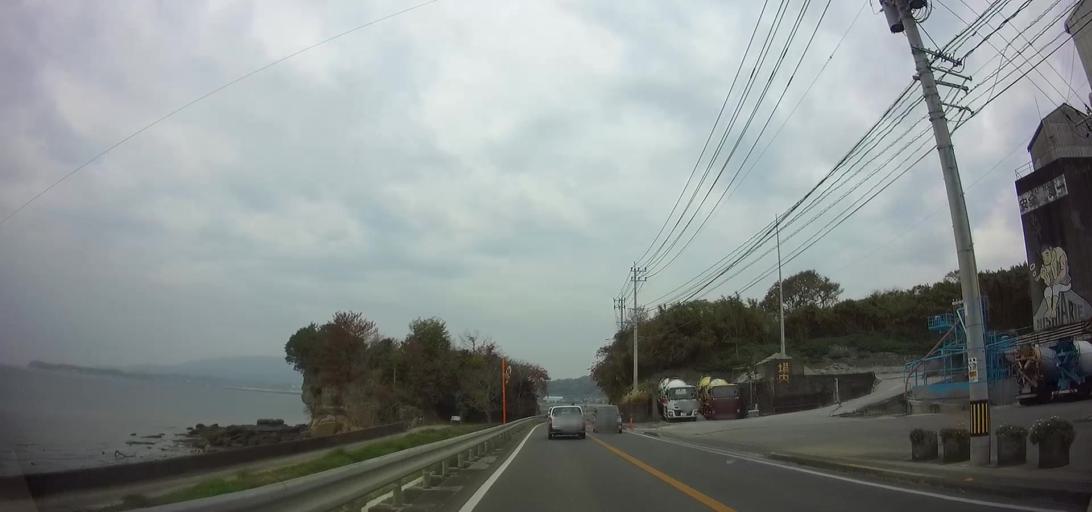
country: JP
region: Nagasaki
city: Shimabara
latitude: 32.6531
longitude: 130.2817
